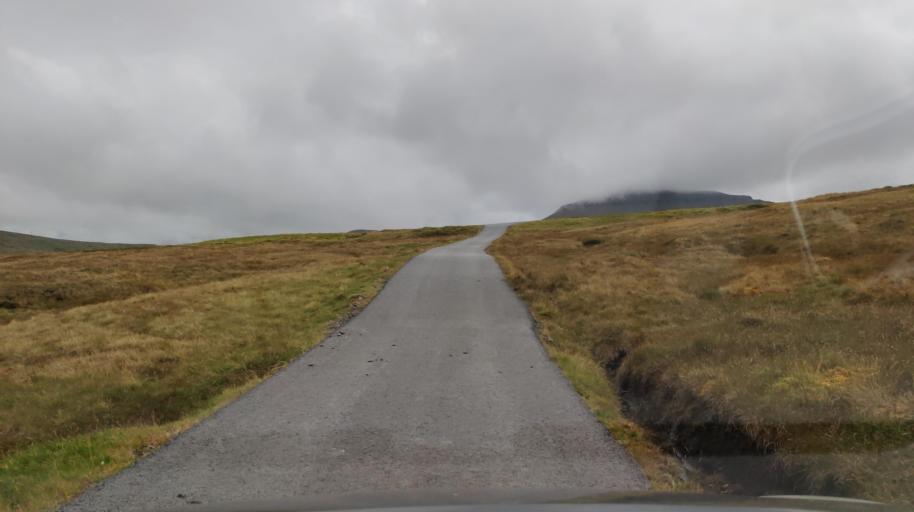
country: FO
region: Streymoy
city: Vestmanna
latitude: 62.1639
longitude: -7.0908
